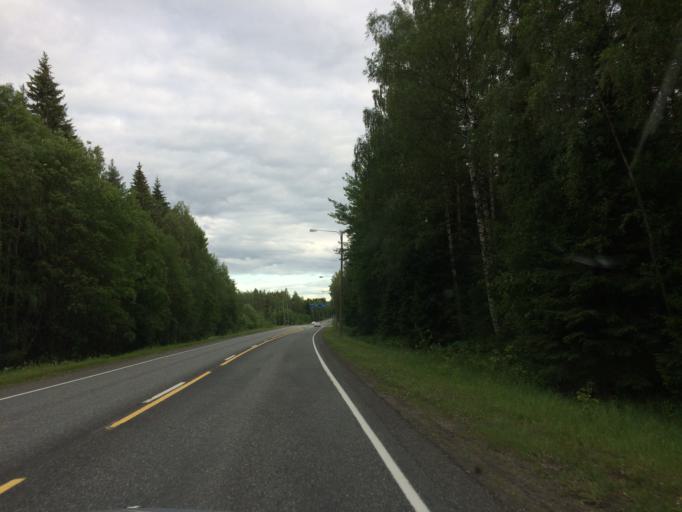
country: FI
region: Haeme
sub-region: Haemeenlinna
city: Haemeenlinna
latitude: 60.9437
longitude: 24.5169
